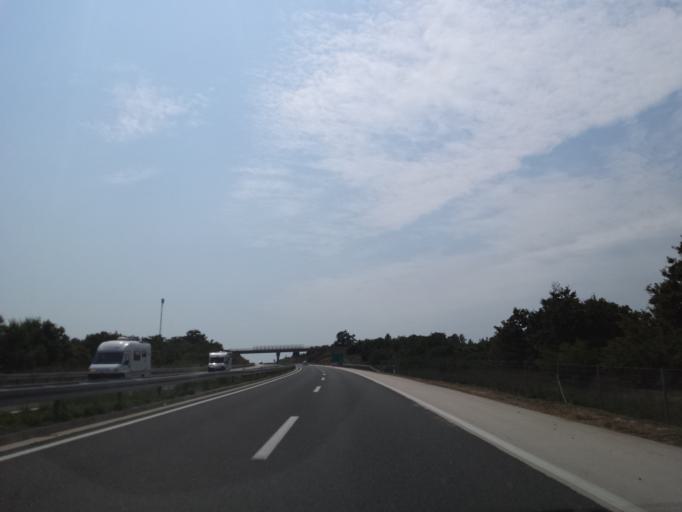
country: HR
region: Zadarska
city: Posedarje
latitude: 44.2100
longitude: 15.4462
